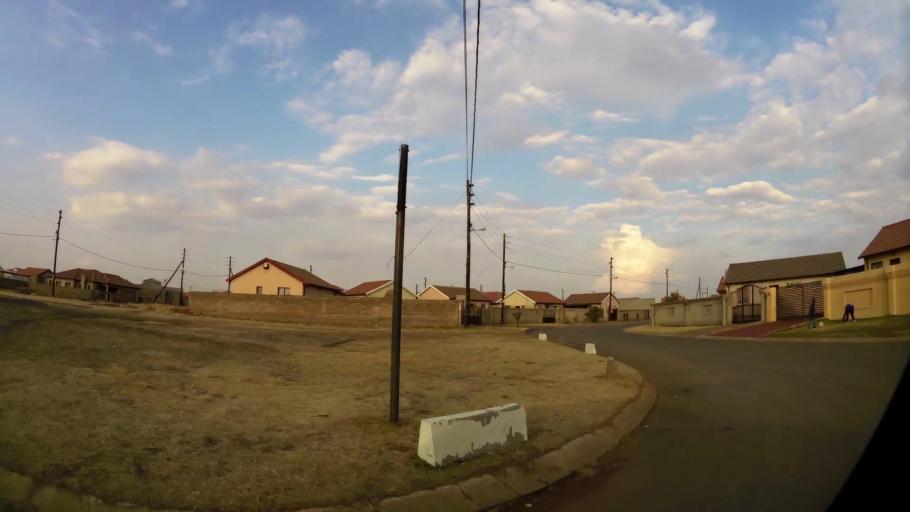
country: ZA
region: Gauteng
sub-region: Sedibeng District Municipality
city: Vanderbijlpark
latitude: -26.6100
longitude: 27.8128
